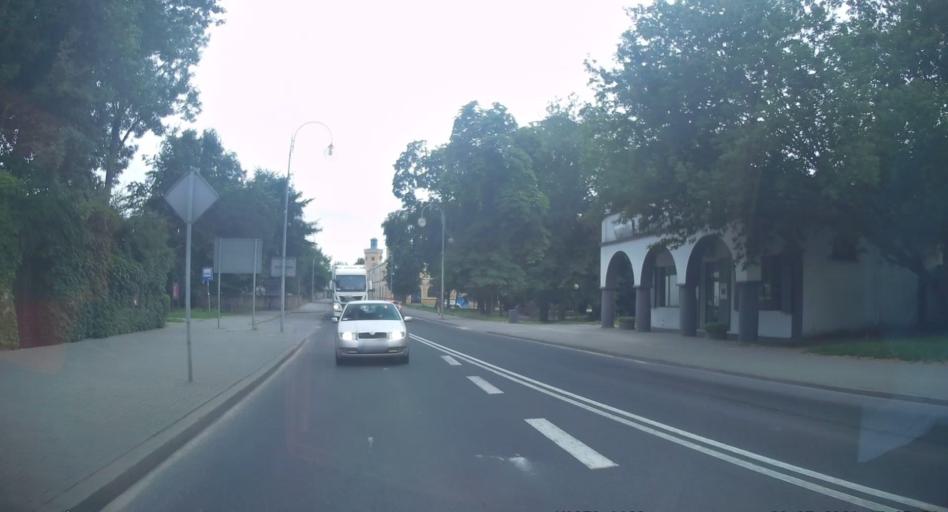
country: PL
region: Lodz Voivodeship
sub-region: Powiat radomszczanski
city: Radomsko
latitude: 51.0696
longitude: 19.4450
